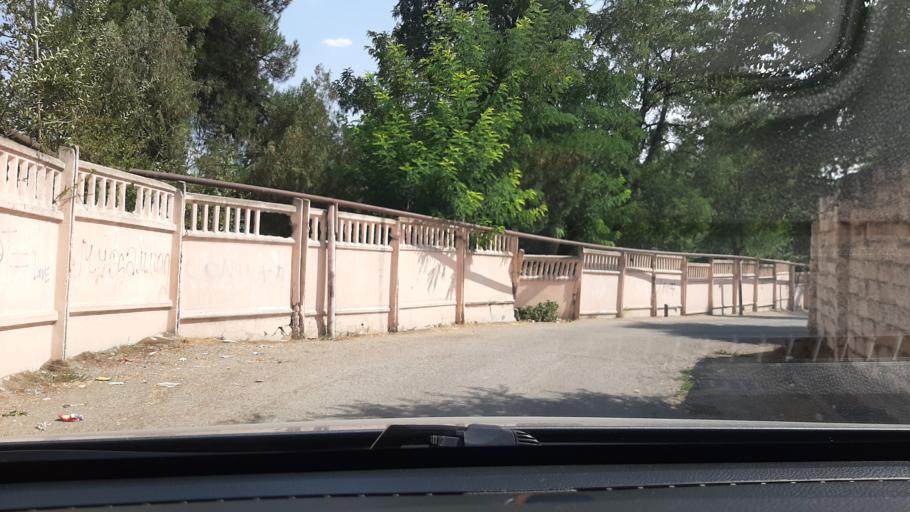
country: TJ
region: Dushanbe
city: Dushanbe
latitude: 38.5679
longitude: 68.8159
